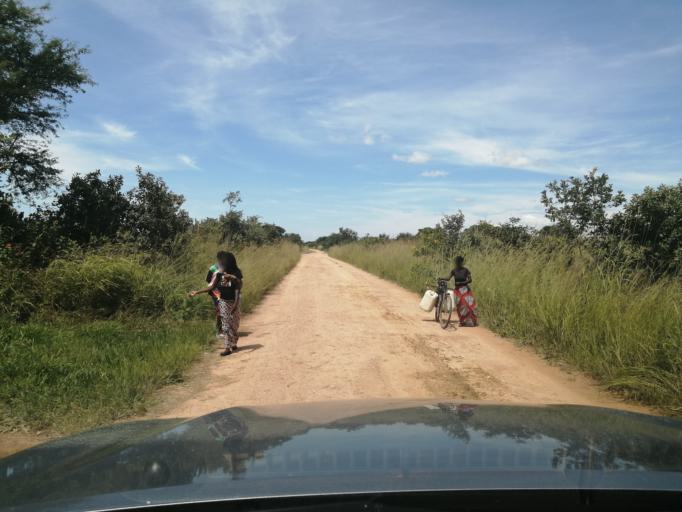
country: ZM
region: Central
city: Chibombo
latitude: -15.0234
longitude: 27.8293
